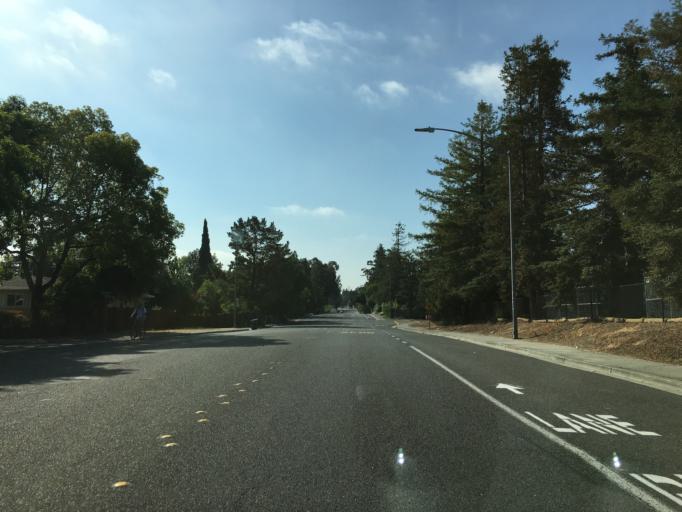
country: US
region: California
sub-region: San Mateo County
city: West Menlo Park
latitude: 37.4471
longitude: -122.2293
